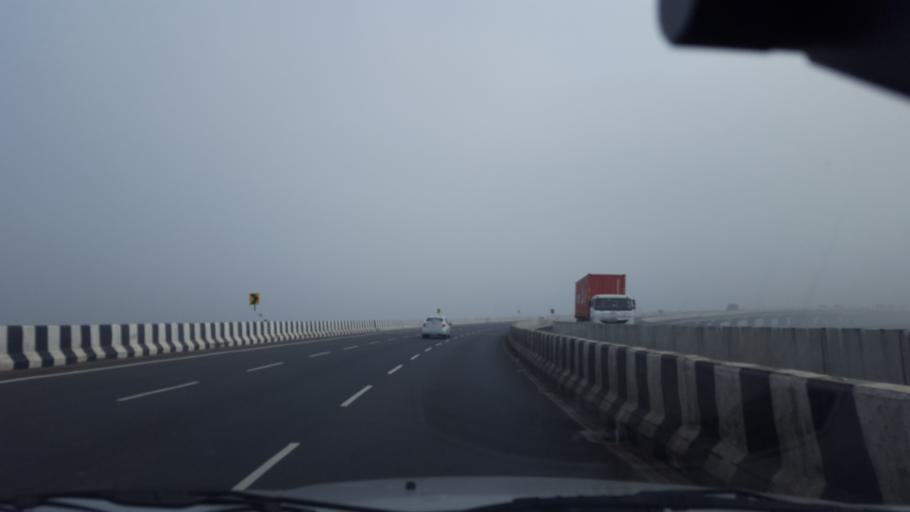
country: IN
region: Andhra Pradesh
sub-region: Prakasam
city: Ongole
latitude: 15.4703
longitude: 80.0487
